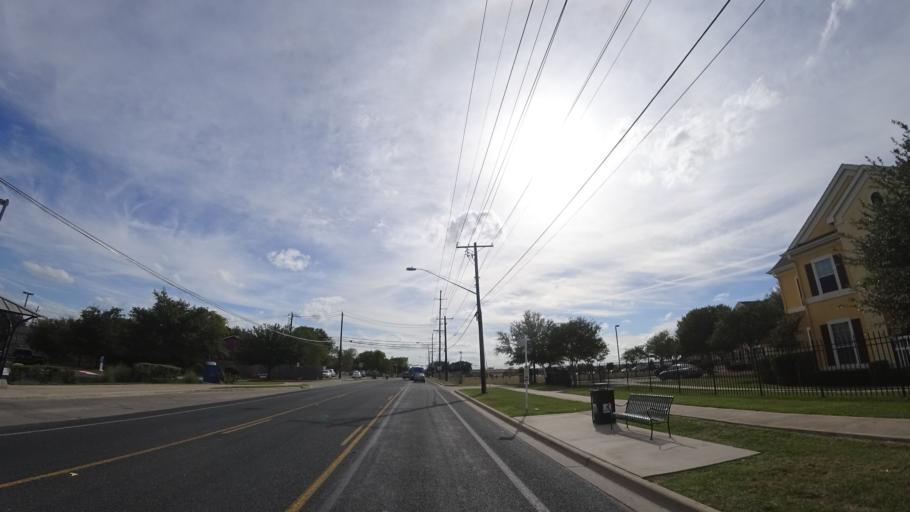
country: US
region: Texas
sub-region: Travis County
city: Austin
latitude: 30.2047
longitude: -97.7531
